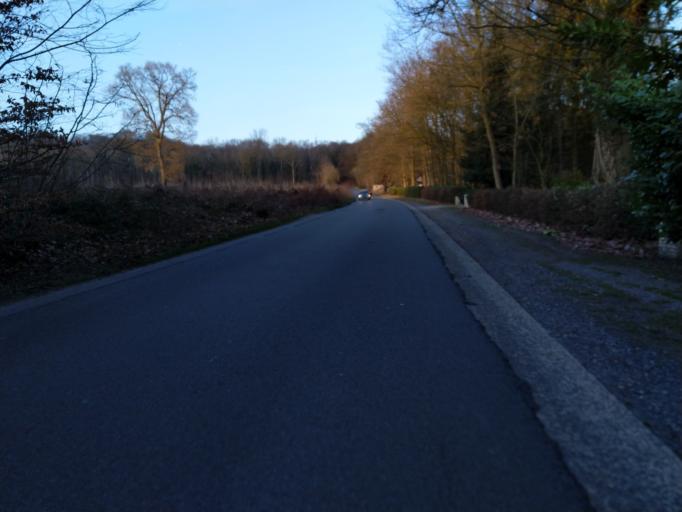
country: BE
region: Wallonia
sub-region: Province du Hainaut
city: Mons
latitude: 50.4935
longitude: 3.9539
